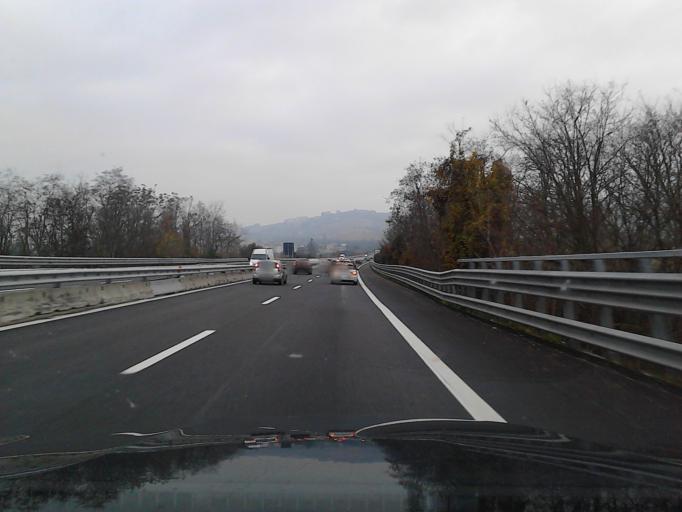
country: IT
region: Abruzzo
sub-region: Provincia di Teramo
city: Alba Adriatica
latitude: 42.8339
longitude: 13.9056
